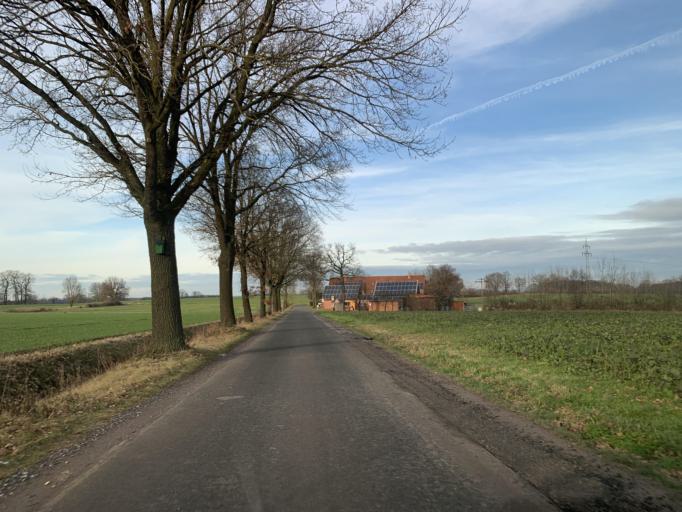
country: DE
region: North Rhine-Westphalia
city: Ludinghausen
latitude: 51.7797
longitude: 7.3800
